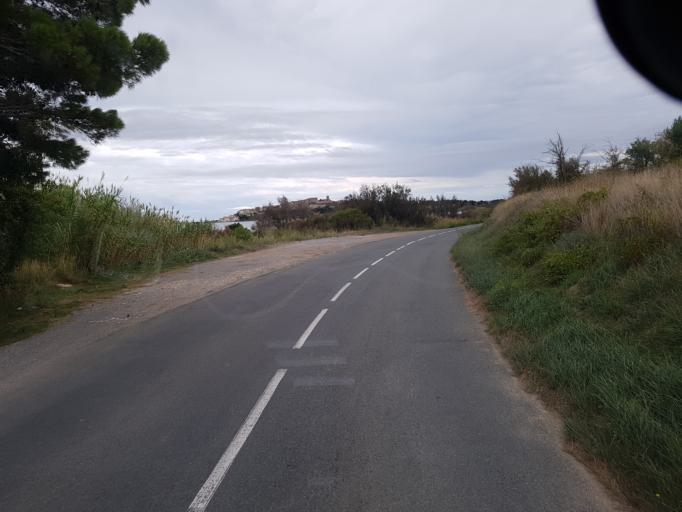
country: FR
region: Languedoc-Roussillon
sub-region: Departement de l'Aude
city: Narbonne
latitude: 43.1333
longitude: 2.9861
